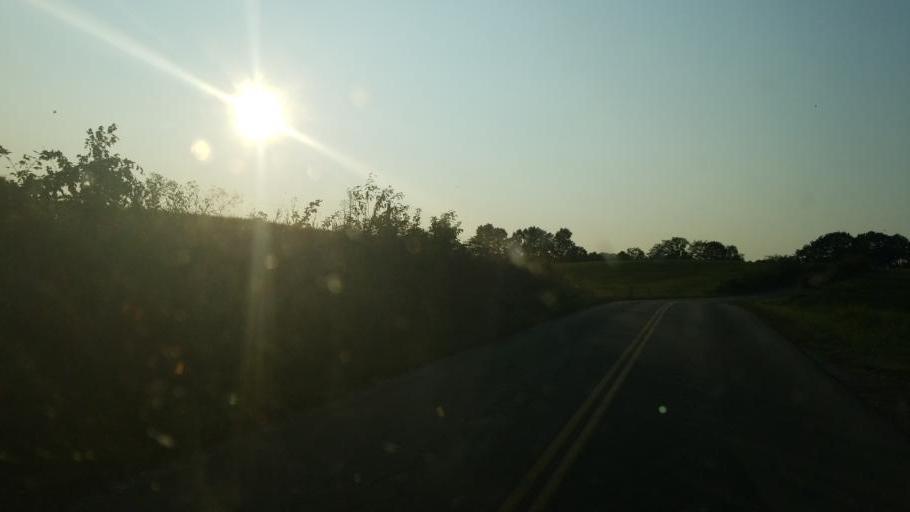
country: US
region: Ohio
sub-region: Wayne County
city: Shreve
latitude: 40.6628
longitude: -81.9677
